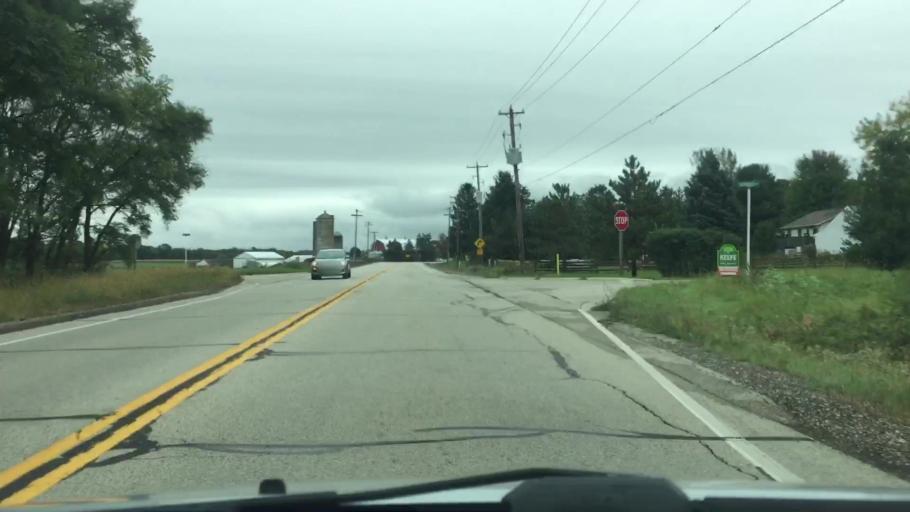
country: US
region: Wisconsin
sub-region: Jefferson County
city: Palmyra
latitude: 42.7822
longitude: -88.5570
